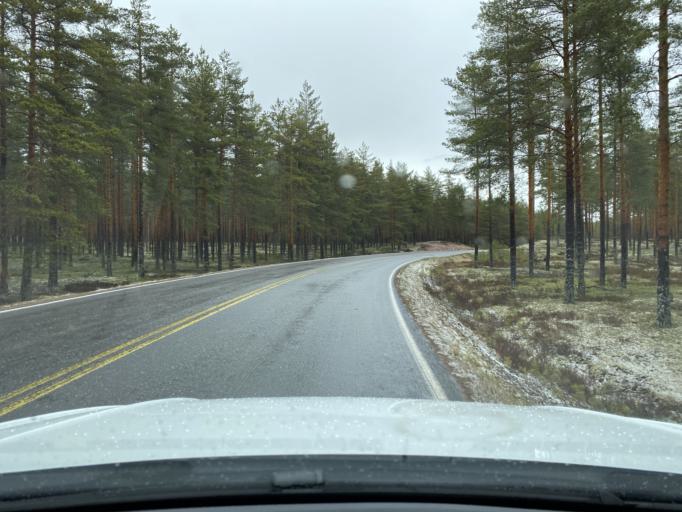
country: FI
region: Satakunta
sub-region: Pori
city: Vampula
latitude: 60.9655
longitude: 22.6749
